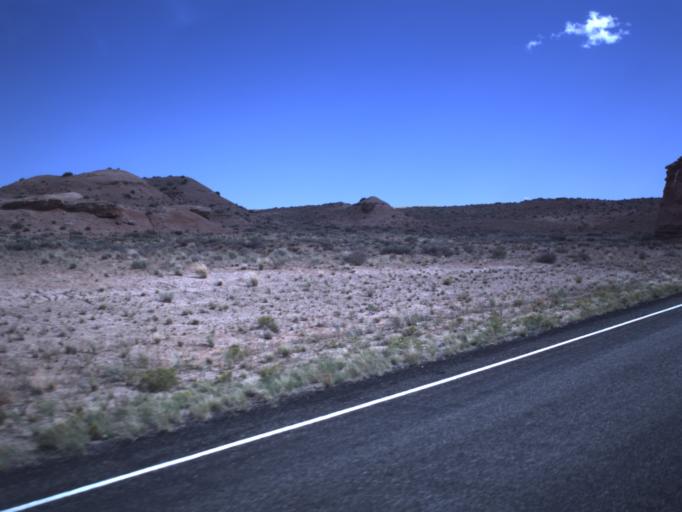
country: US
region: Utah
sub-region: Emery County
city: Ferron
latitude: 38.3569
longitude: -110.6975
